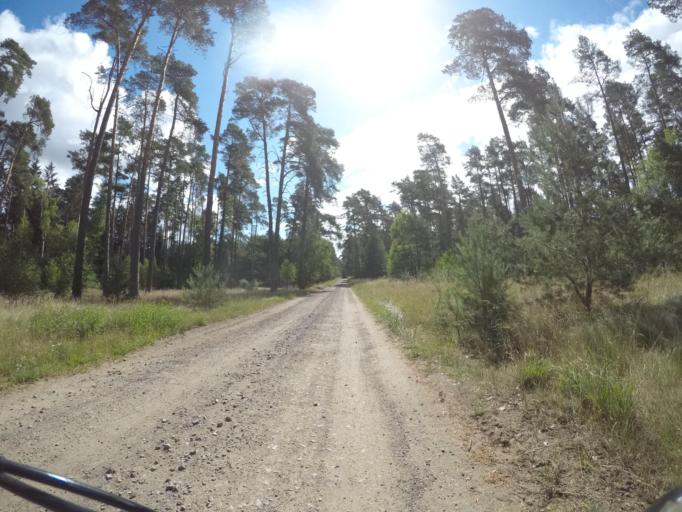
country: DE
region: Lower Saxony
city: Hitzacker
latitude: 53.2332
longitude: 11.0162
